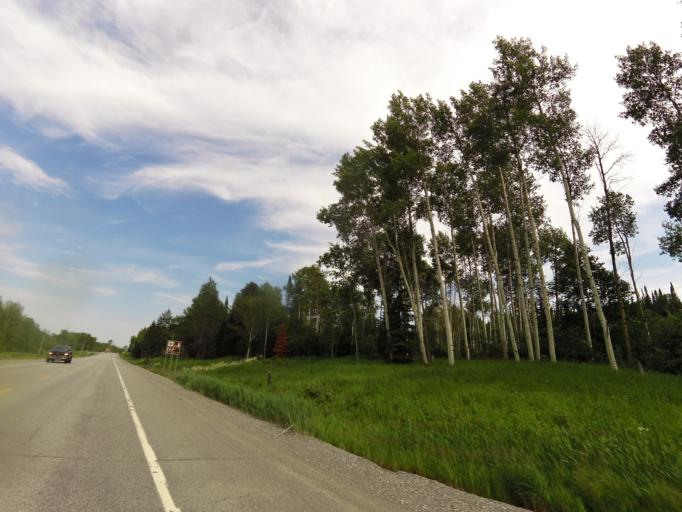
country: CA
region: Quebec
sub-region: Abitibi-Temiscamingue
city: Malartic
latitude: 48.2335
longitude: -78.4192
